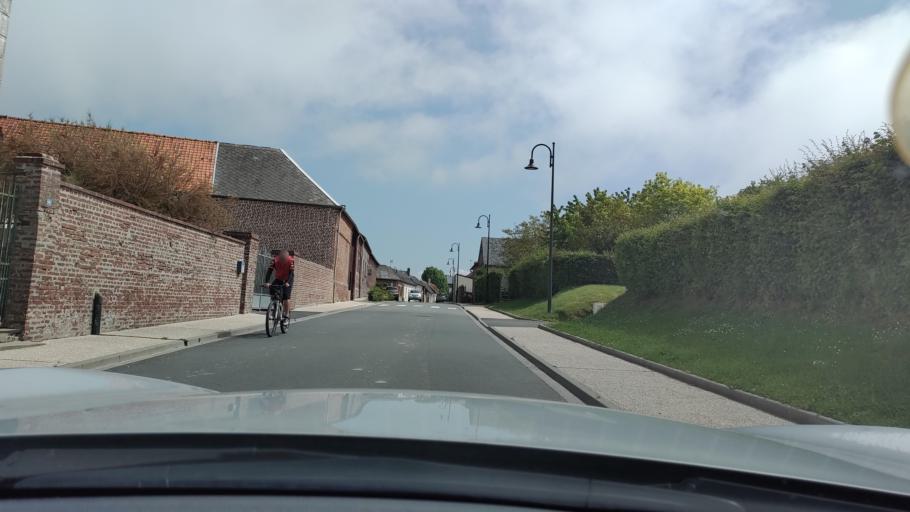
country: FR
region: Picardie
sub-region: Departement de la Somme
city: Ault
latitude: 50.0736
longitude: 1.4587
